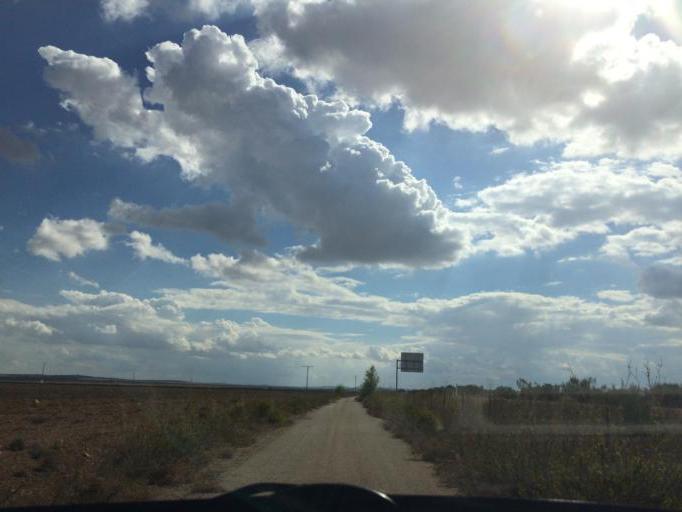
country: ES
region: Castille-La Mancha
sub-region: Provincia de Albacete
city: Albacete
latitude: 38.9592
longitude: -1.8207
